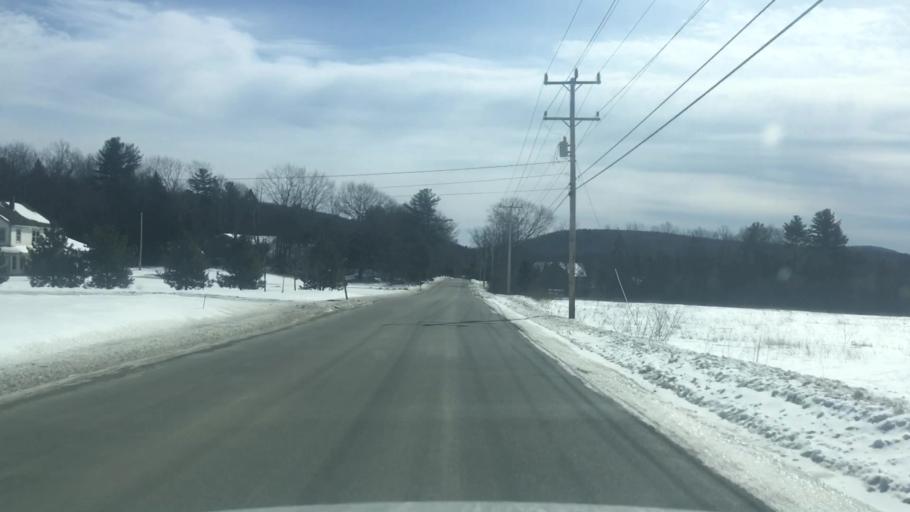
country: US
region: Maine
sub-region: Penobscot County
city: Holden
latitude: 44.7444
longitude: -68.6306
